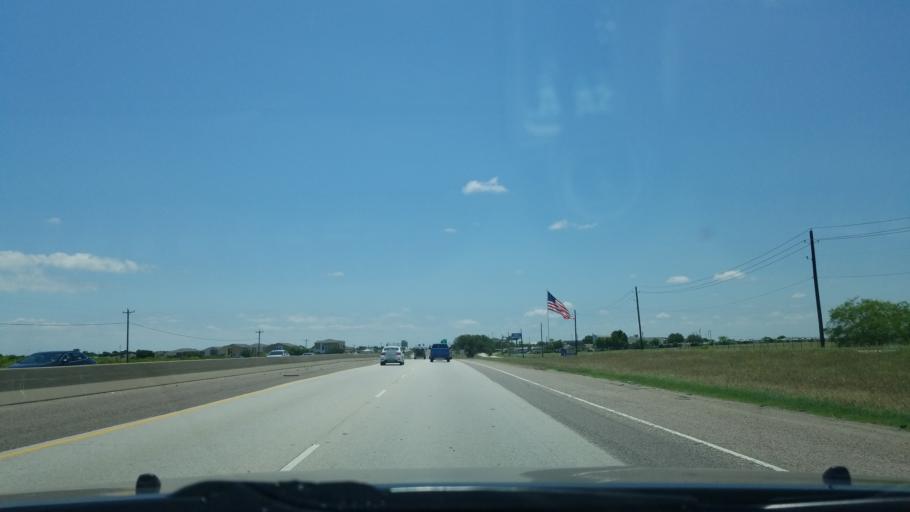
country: US
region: Texas
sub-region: Denton County
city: Denton
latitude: 33.2505
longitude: -97.1774
